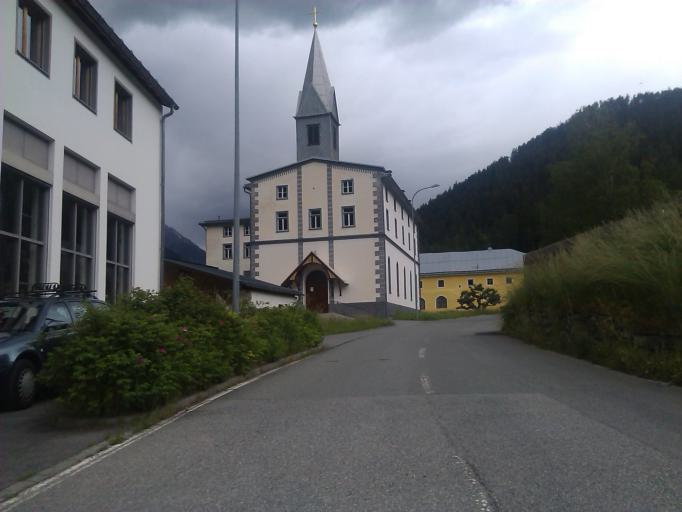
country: AT
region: Tyrol
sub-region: Politischer Bezirk Landeck
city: Nauders
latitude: 46.8841
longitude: 10.4634
